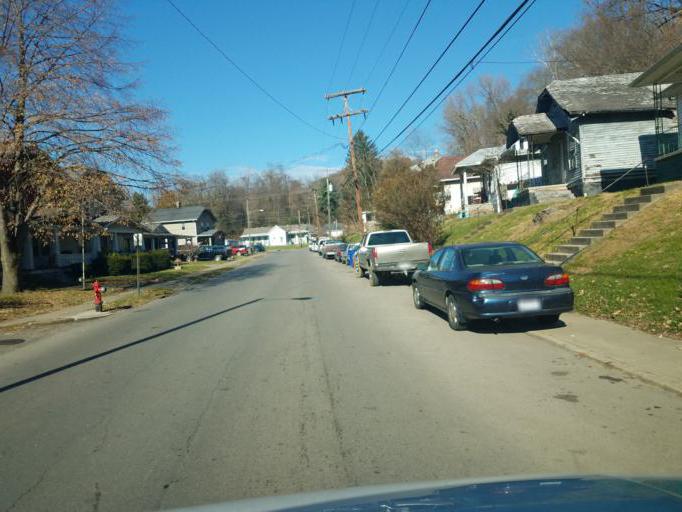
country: US
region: Kentucky
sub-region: Greenup County
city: South Shore
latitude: 38.7432
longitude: -82.9651
